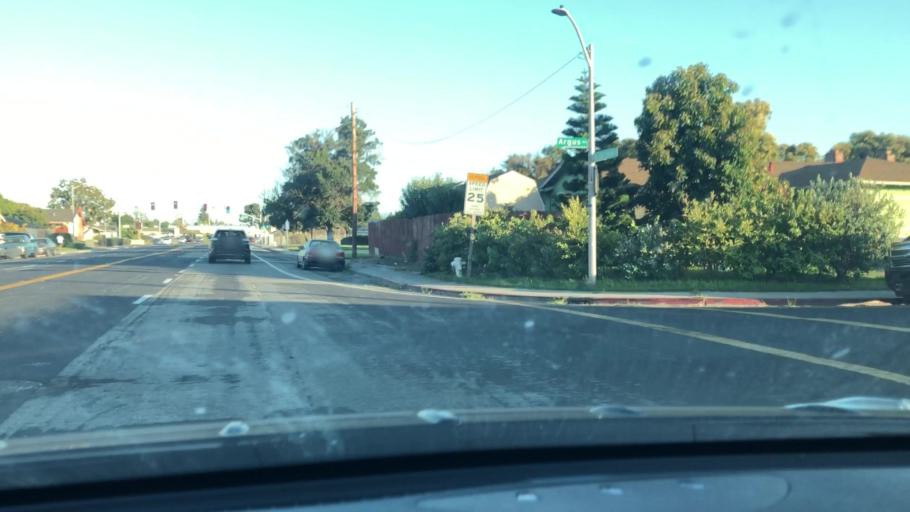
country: US
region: California
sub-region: Santa Clara County
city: Santa Clara
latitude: 37.3909
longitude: -121.9457
